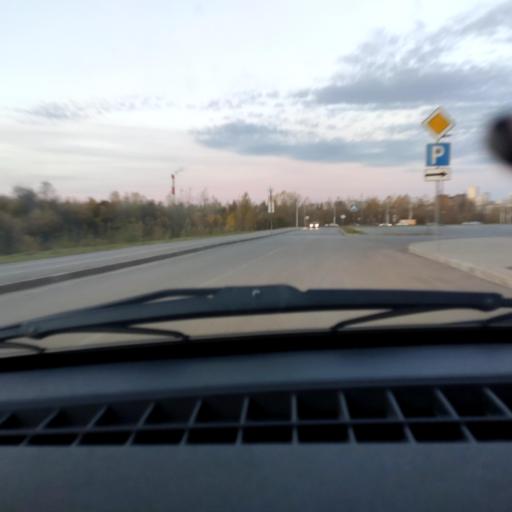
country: RU
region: Bashkortostan
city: Ufa
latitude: 54.7897
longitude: 56.0812
